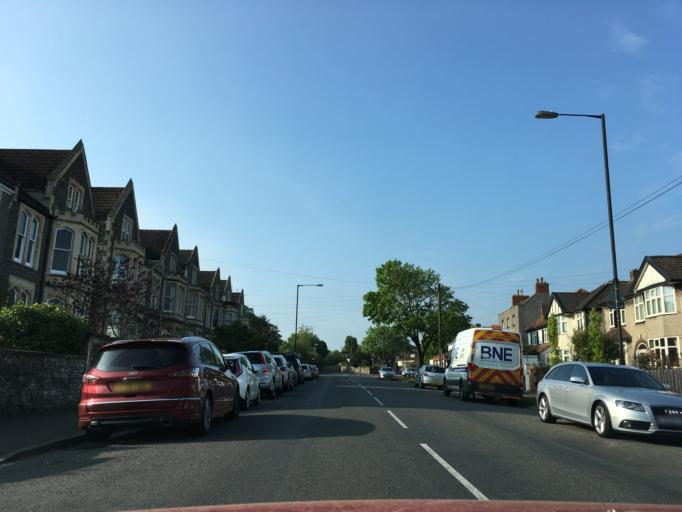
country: GB
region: England
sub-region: Bristol
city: Bristol
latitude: 51.4893
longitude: -2.6170
